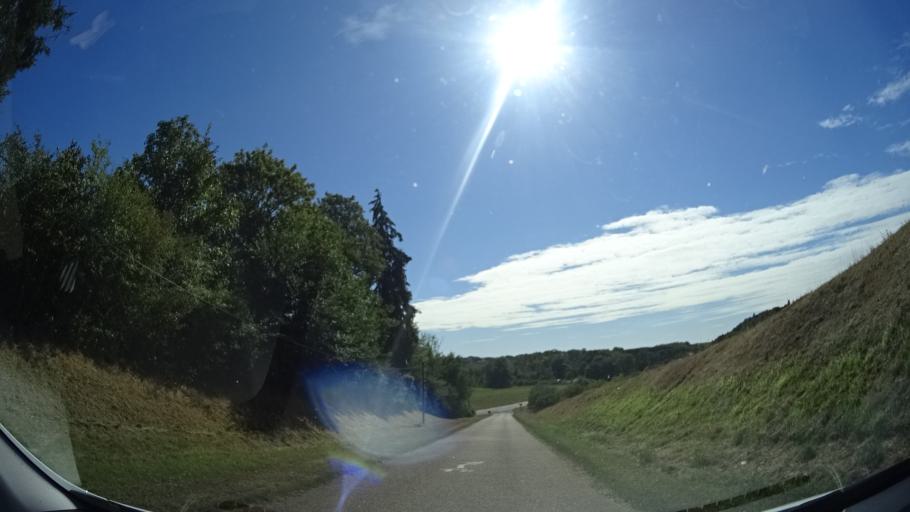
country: FR
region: Centre
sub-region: Departement du Loiret
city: Trigueres
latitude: 47.9366
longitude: 2.9470
